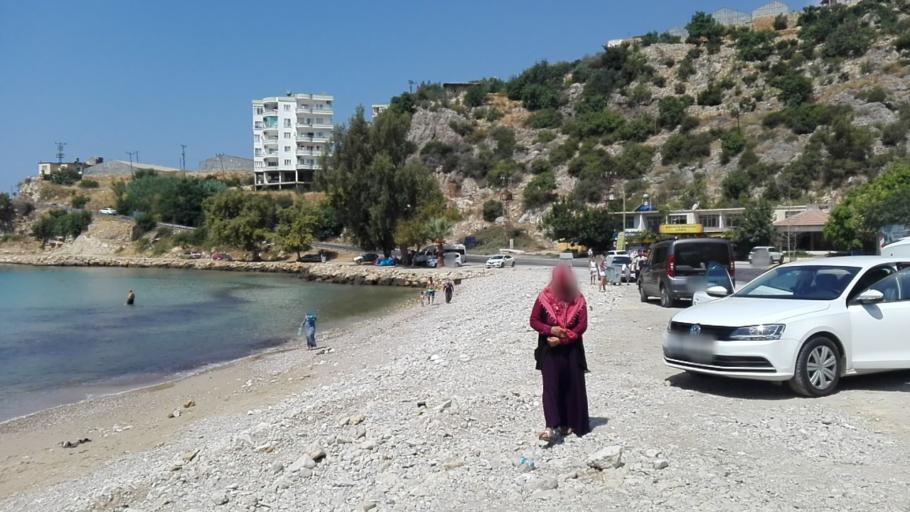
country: TR
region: Mersin
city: Aydincik
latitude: 36.1355
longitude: 33.2961
